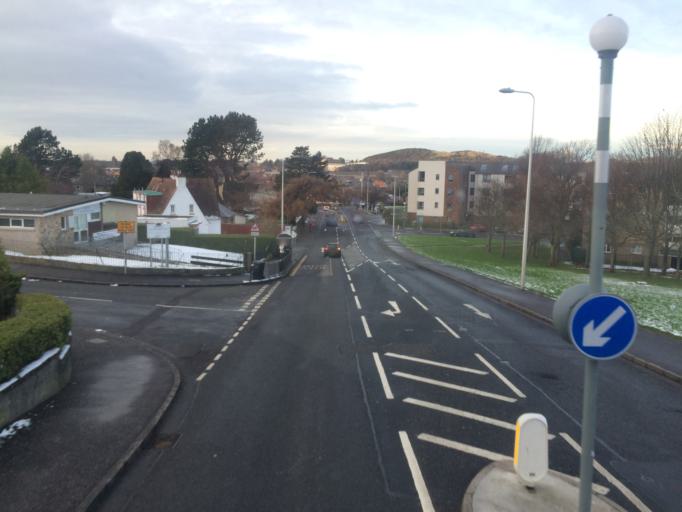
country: GB
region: Scotland
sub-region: Edinburgh
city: Colinton
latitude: 55.9066
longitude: -3.2260
